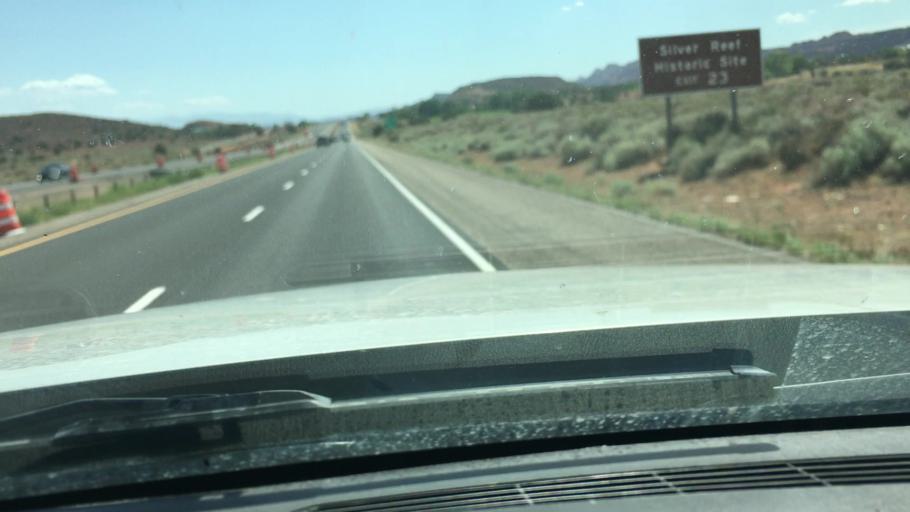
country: US
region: Utah
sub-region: Washington County
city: Toquerville
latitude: 37.2529
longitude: -113.3399
